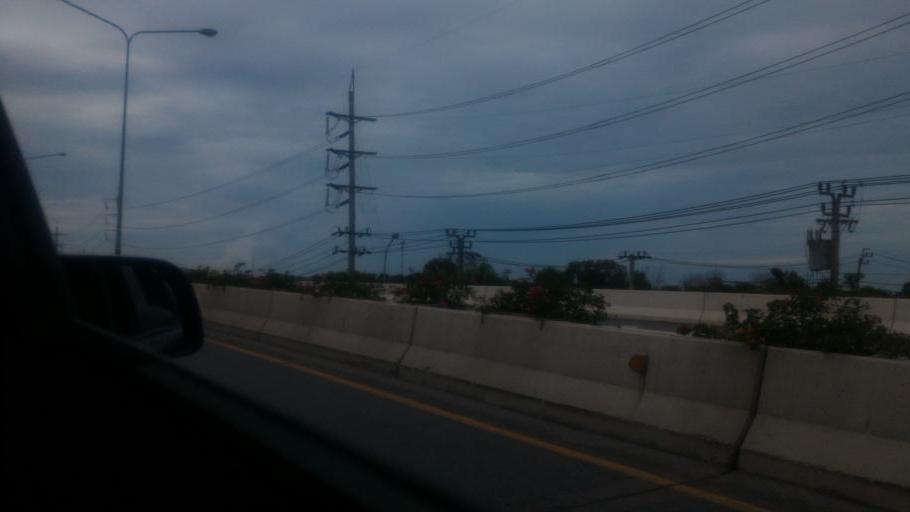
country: TH
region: Bangkok
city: Bang Khun Thian
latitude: 13.6243
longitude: 100.4357
